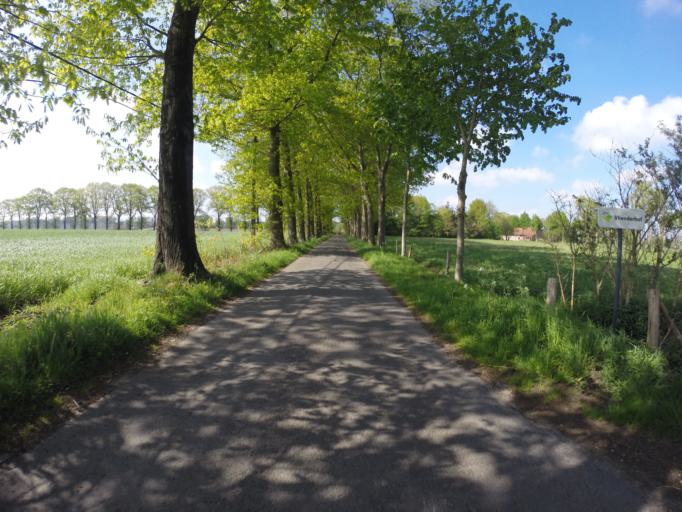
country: BE
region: Flanders
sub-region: Provincie West-Vlaanderen
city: Beernem
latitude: 51.1027
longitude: 3.3374
